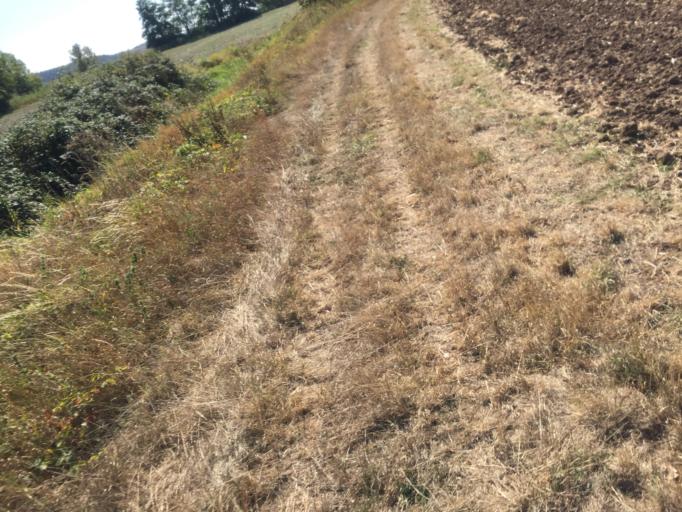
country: DE
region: Hesse
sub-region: Regierungsbezirk Giessen
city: Hungen
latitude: 50.4437
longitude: 8.9053
